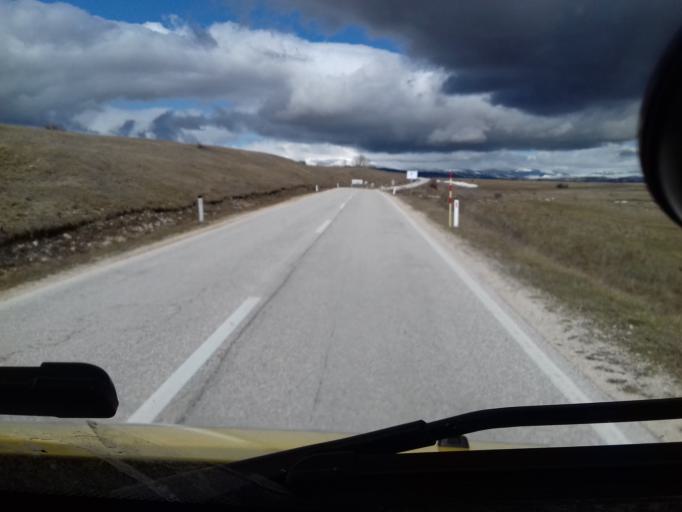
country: BA
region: Federation of Bosnia and Herzegovina
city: Dreznica
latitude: 43.6136
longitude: 17.2666
